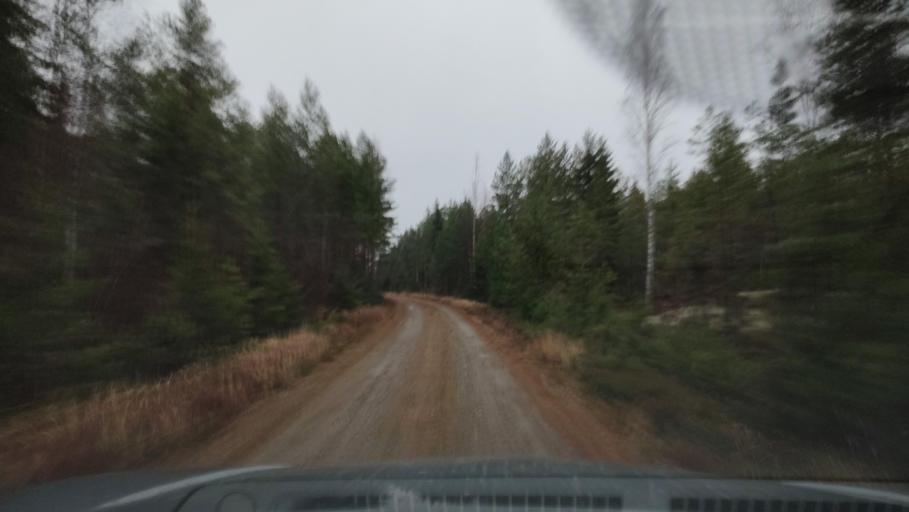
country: FI
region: Southern Ostrobothnia
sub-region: Suupohja
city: Karijoki
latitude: 62.1576
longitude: 21.5896
